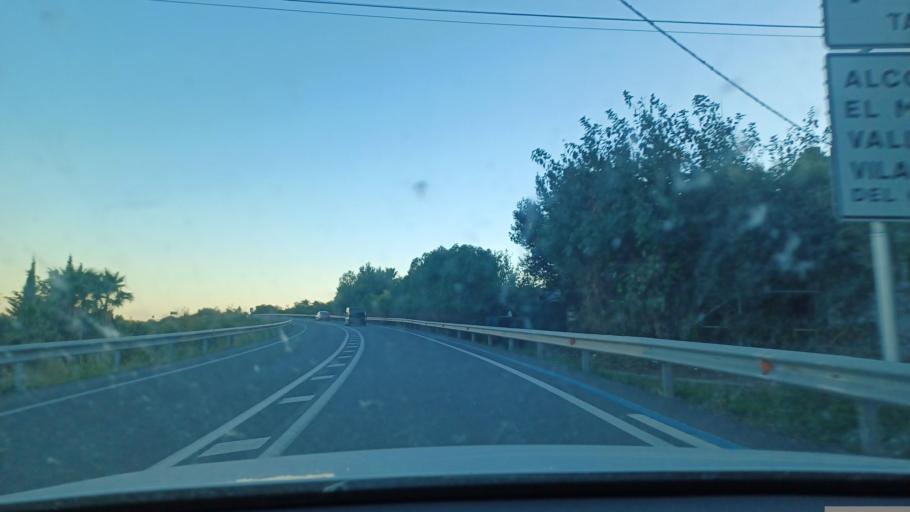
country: ES
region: Catalonia
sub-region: Provincia de Tarragona
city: Alcover
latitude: 41.2687
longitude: 1.1749
